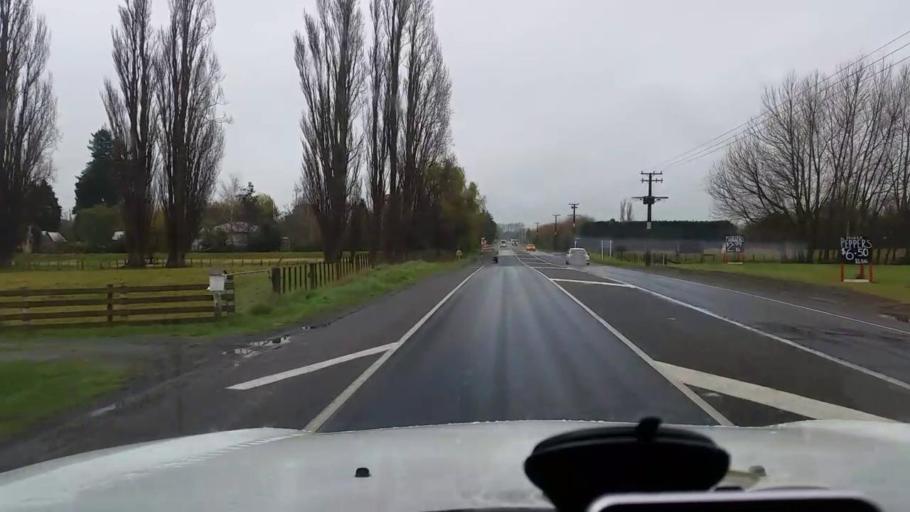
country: NZ
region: Wellington
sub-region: Masterton District
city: Masterton
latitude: -41.0733
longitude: 175.4684
